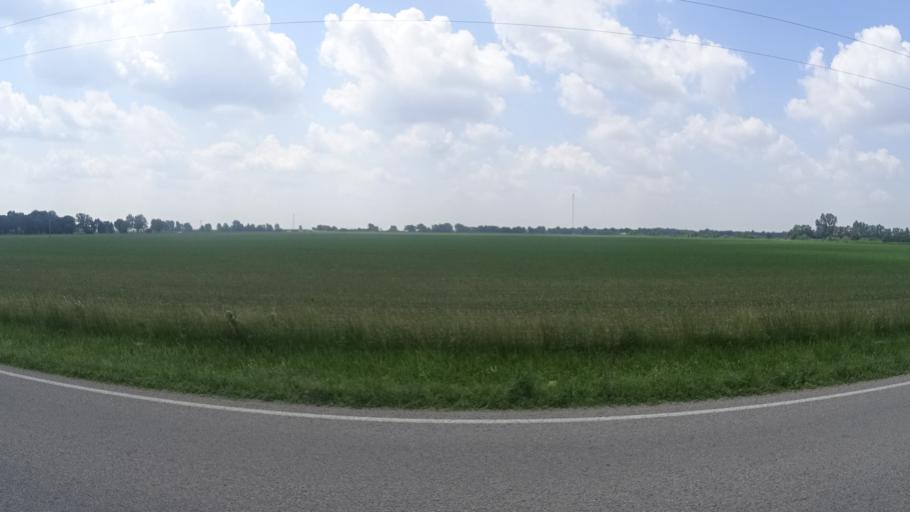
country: US
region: Ohio
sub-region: Huron County
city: Monroeville
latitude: 41.3234
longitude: -82.6954
